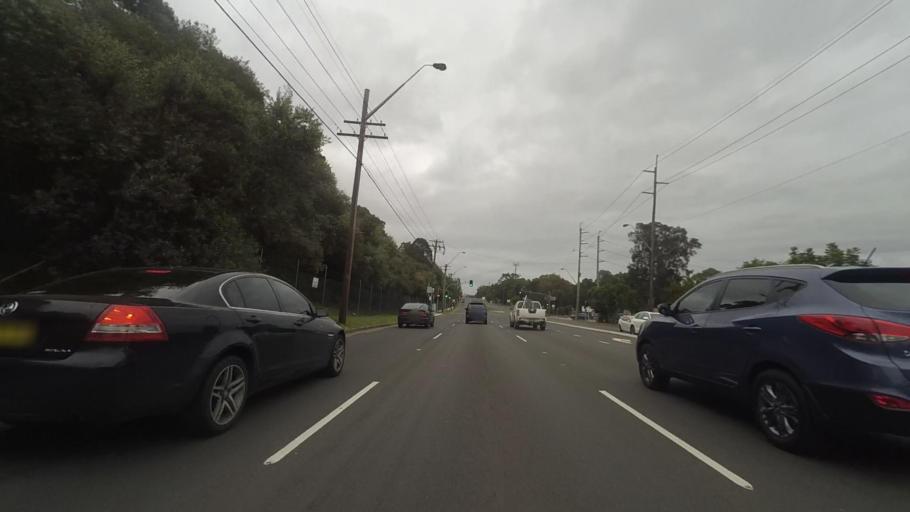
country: AU
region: New South Wales
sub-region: Auburn
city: Berala
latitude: -33.8925
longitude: 151.0385
